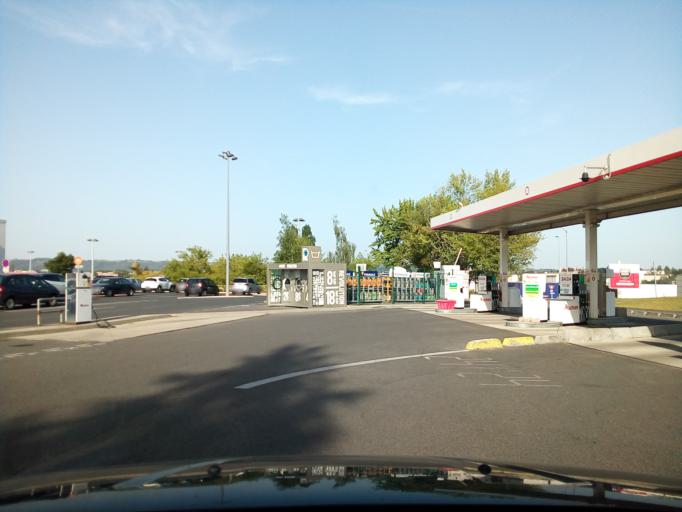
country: FR
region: Auvergne
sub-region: Departement de l'Allier
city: Montlucon
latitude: 46.3384
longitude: 2.5671
